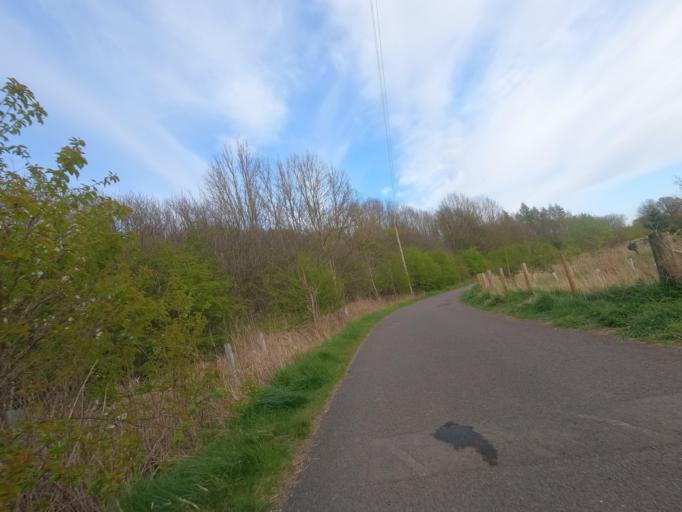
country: GB
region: England
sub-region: Newcastle upon Tyne
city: Hazlerigg
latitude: 55.0587
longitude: -1.6327
